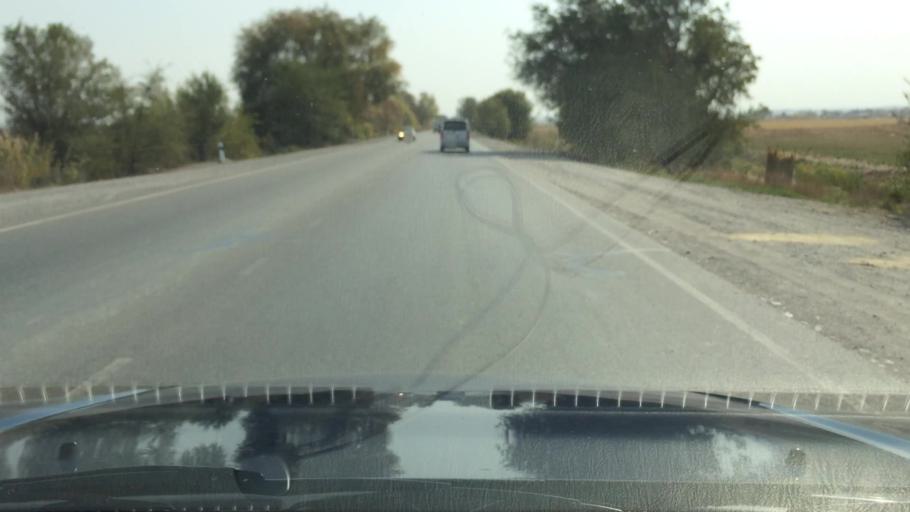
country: KG
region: Chuy
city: Lebedinovka
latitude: 42.9291
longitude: 74.6938
